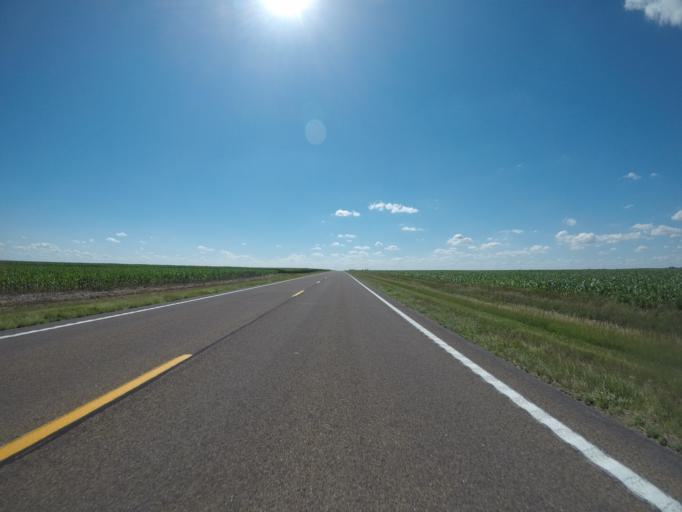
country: US
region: Nebraska
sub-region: Chase County
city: Imperial
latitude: 40.5372
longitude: -101.9510
